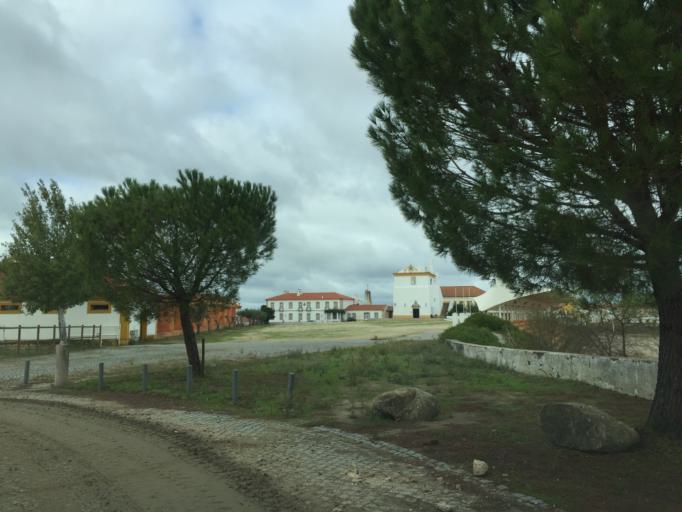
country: PT
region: Portalegre
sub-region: Alter do Chao
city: Alter do Chao
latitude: 39.2214
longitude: -7.6850
